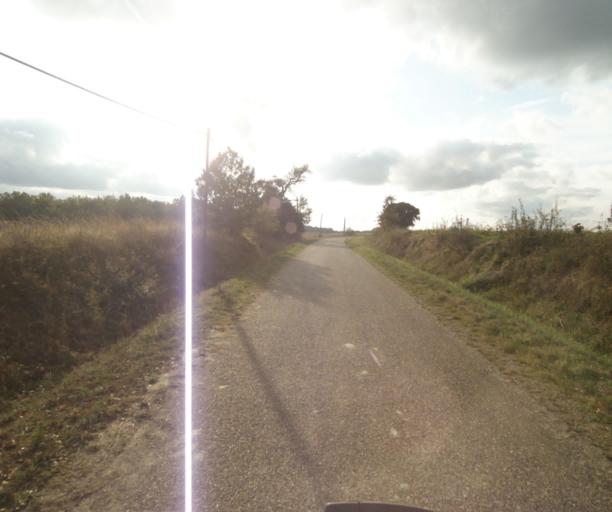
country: FR
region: Midi-Pyrenees
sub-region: Departement de la Haute-Garonne
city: Launac
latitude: 43.8246
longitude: 1.1109
